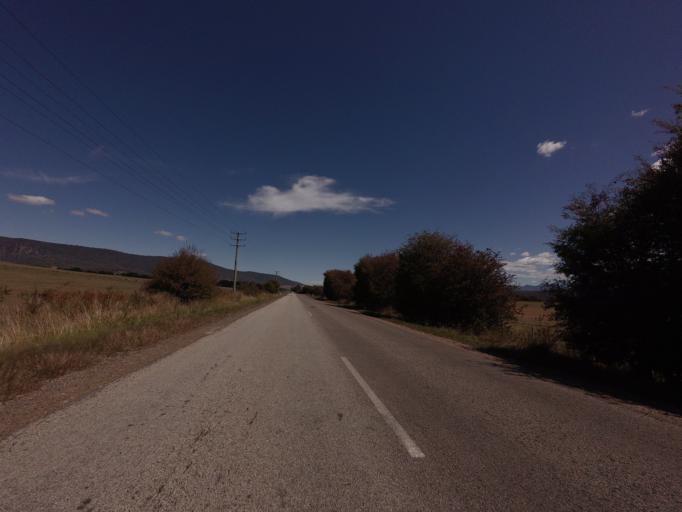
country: AU
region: Tasmania
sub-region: Break O'Day
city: St Helens
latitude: -41.6235
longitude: 147.9972
